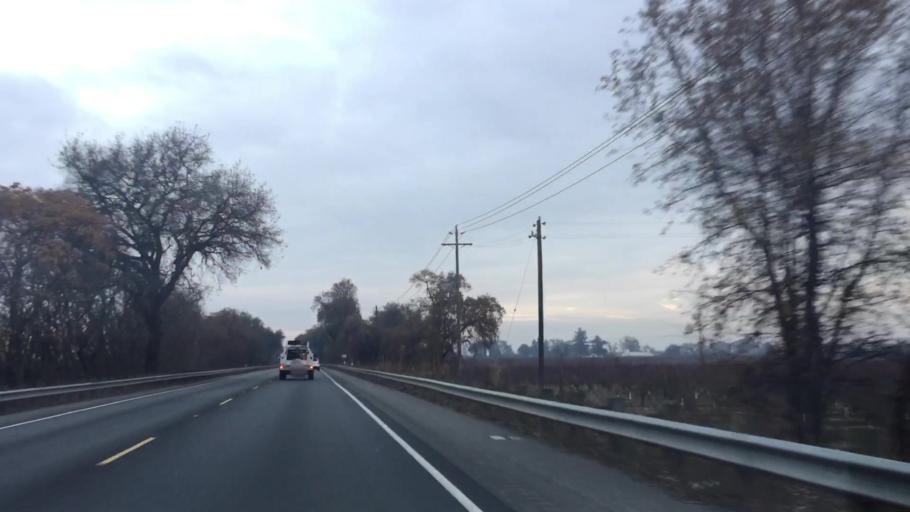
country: US
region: California
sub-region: Sutter County
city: Live Oak
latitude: 39.3130
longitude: -121.5956
